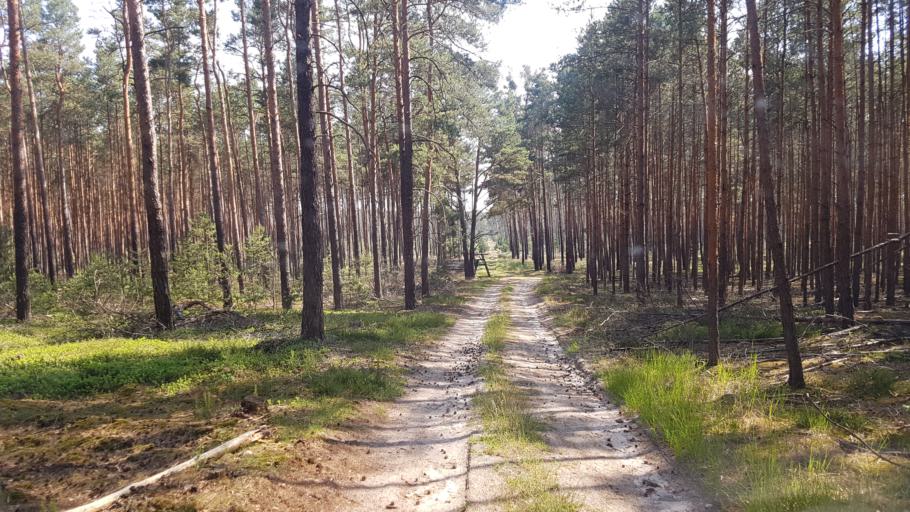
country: DE
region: Brandenburg
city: Trobitz
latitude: 51.6401
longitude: 13.4311
